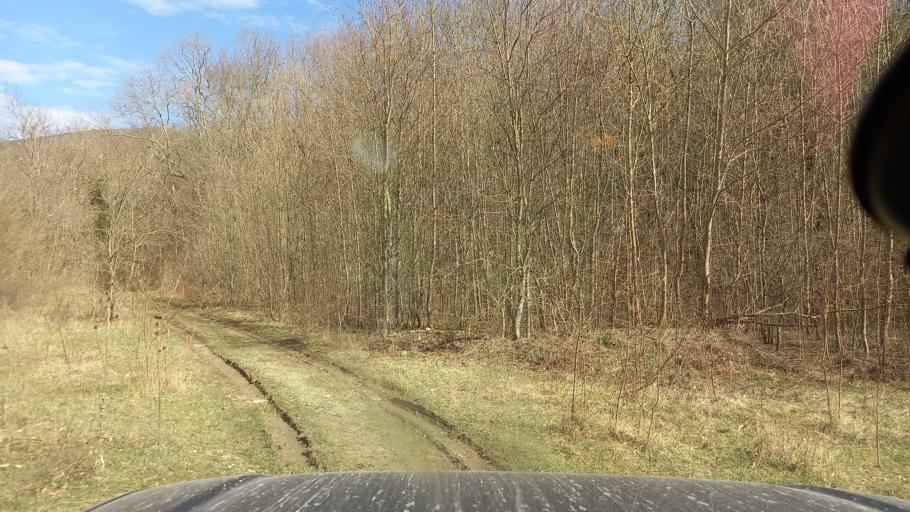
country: RU
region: Krasnodarskiy
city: Arkhipo-Osipovka
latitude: 44.3783
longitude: 38.5973
